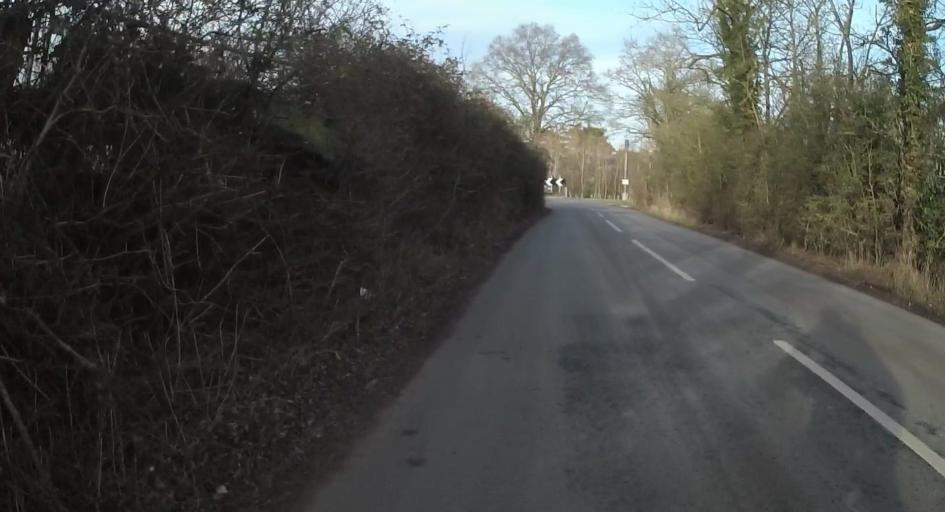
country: GB
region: England
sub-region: West Berkshire
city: Stratfield Mortimer
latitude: 51.4026
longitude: -1.0298
